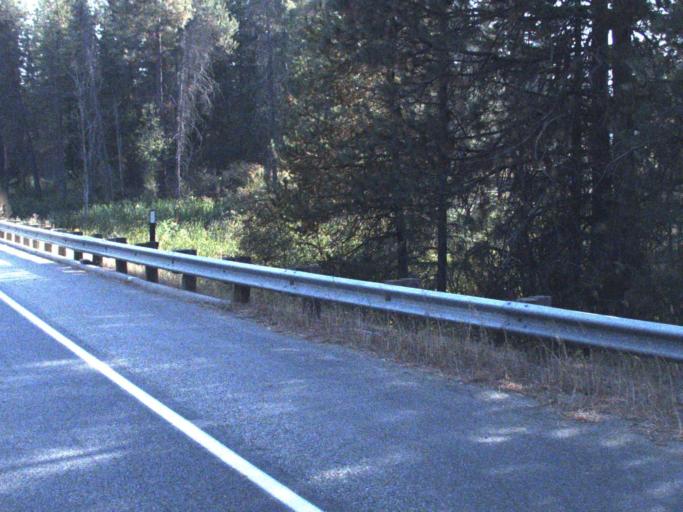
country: US
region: Washington
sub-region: Spokane County
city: Deer Park
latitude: 47.9997
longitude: -117.3496
